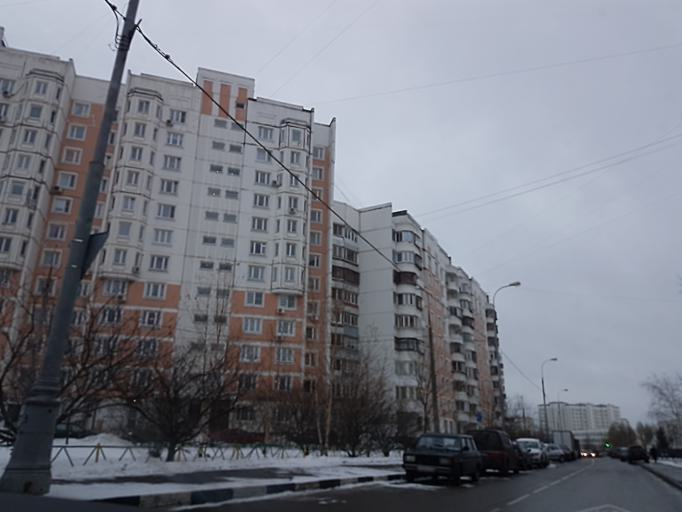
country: RU
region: Moskovskaya
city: Pavshino
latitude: 55.8318
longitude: 37.3509
